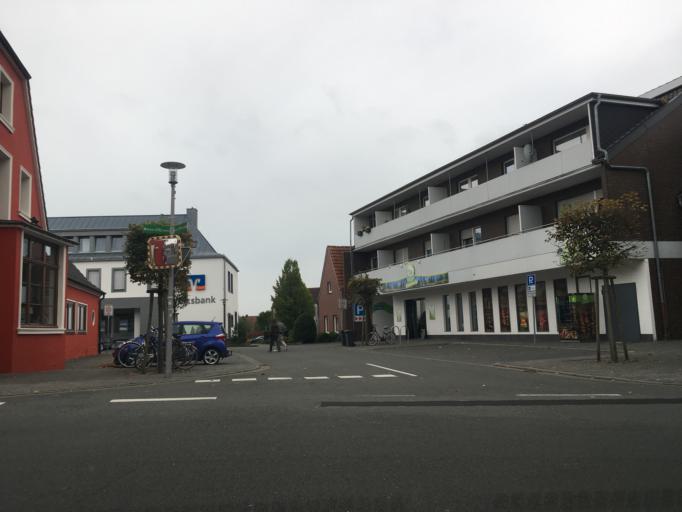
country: DE
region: North Rhine-Westphalia
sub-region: Regierungsbezirk Munster
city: Schoppingen
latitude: 52.0921
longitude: 7.2369
